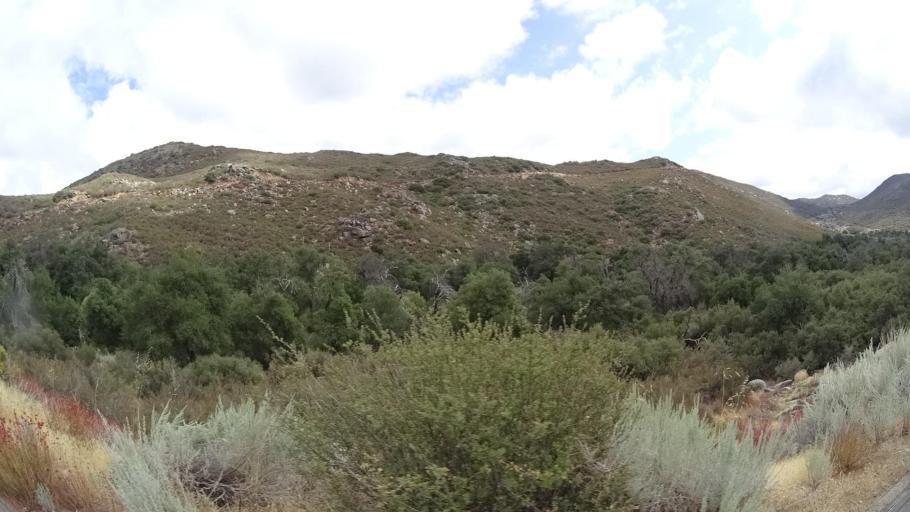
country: US
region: California
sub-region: San Diego County
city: Pine Valley
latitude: 32.7835
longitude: -116.4501
